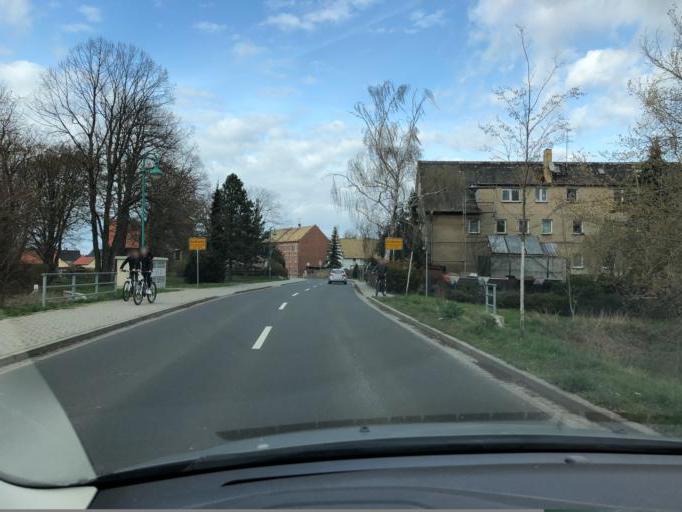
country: DE
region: Saxony
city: Markranstadt
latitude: 51.2816
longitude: 12.2319
